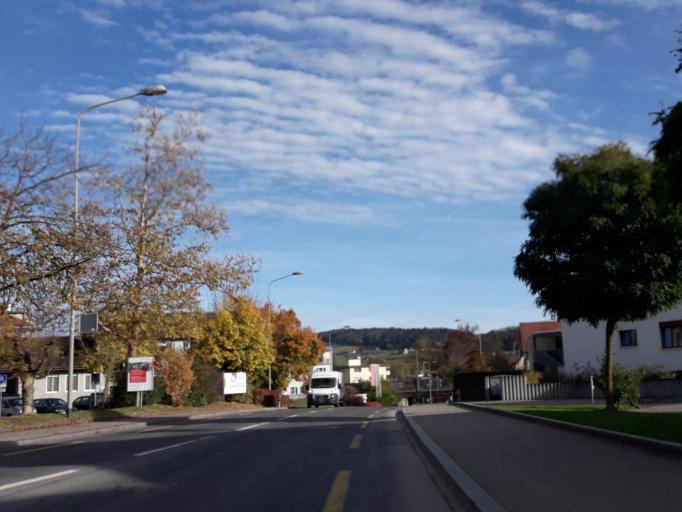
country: CH
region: Zurich
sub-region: Bezirk Buelach
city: Bulach
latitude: 47.5206
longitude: 8.5345
